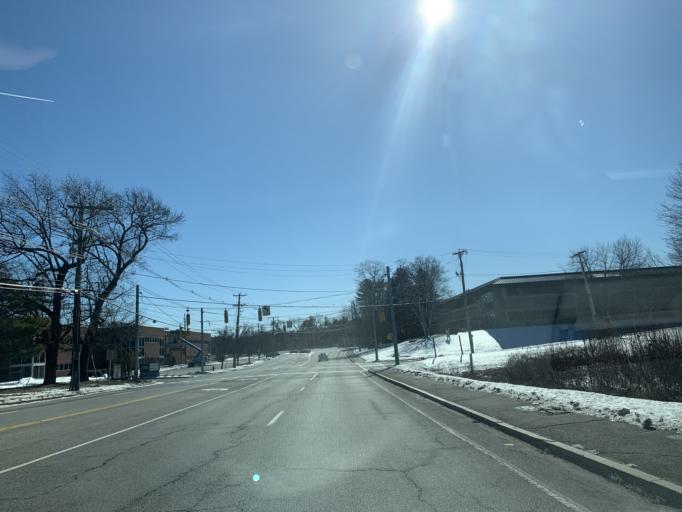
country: US
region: Massachusetts
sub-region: Middlesex County
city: Lowell
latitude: 42.5922
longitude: -71.3180
